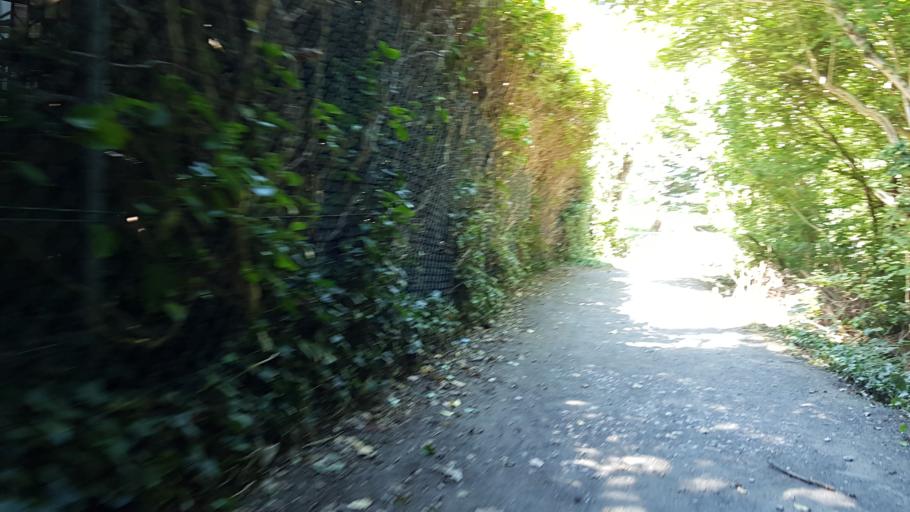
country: GB
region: England
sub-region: Isle of Wight
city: Newport
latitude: 50.6939
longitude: -1.3087
